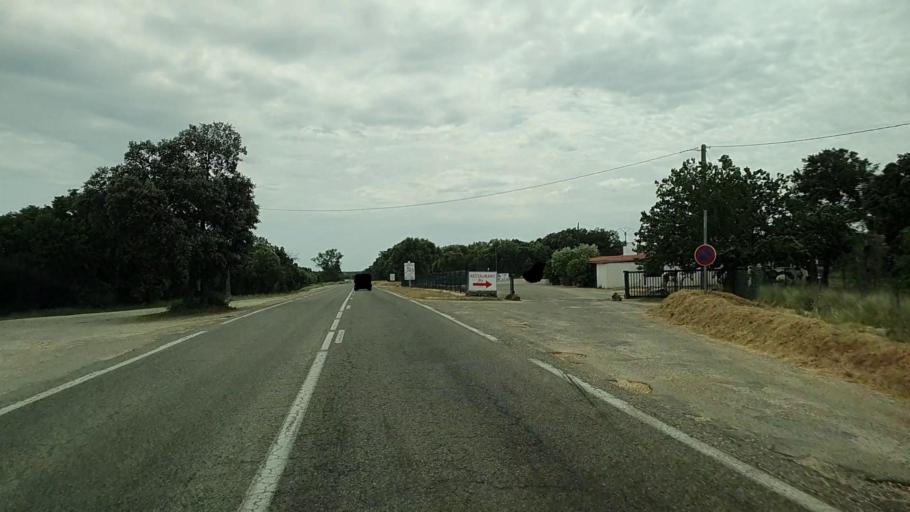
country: FR
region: Languedoc-Roussillon
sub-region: Departement du Gard
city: Connaux
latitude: 44.0540
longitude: 4.5716
